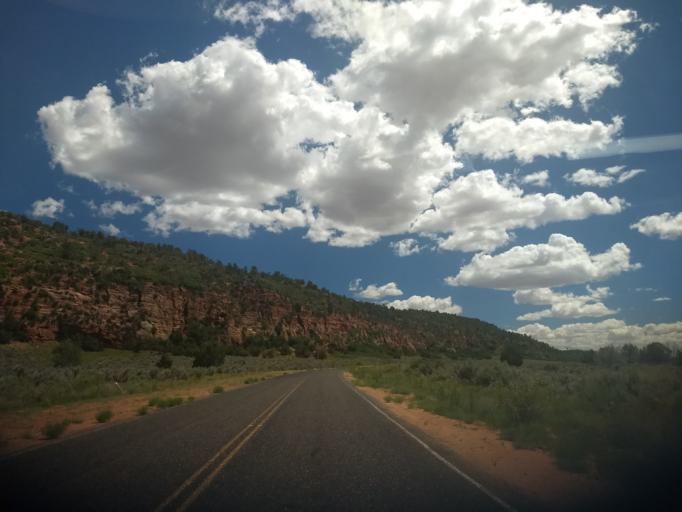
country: US
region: Utah
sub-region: Kane County
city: Kanab
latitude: 37.1047
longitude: -112.6812
